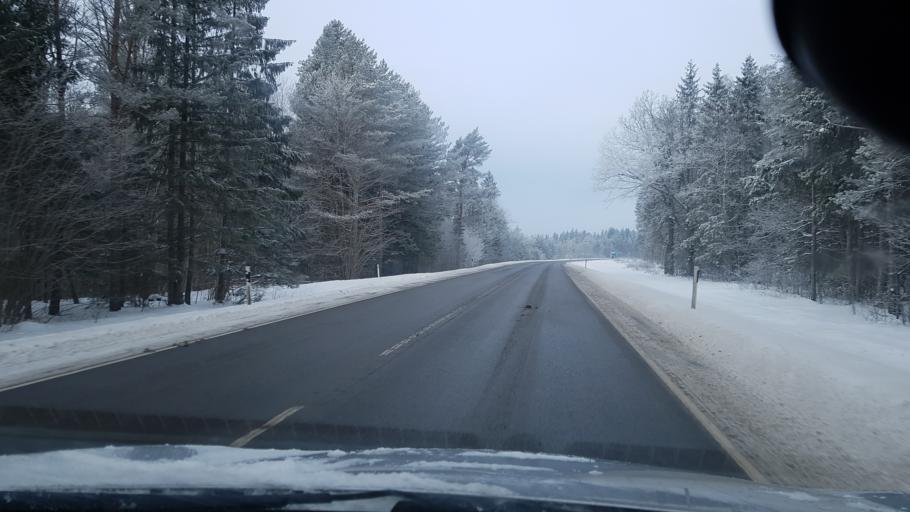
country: EE
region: Harju
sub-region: Keila linn
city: Keila
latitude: 59.3303
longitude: 24.2970
